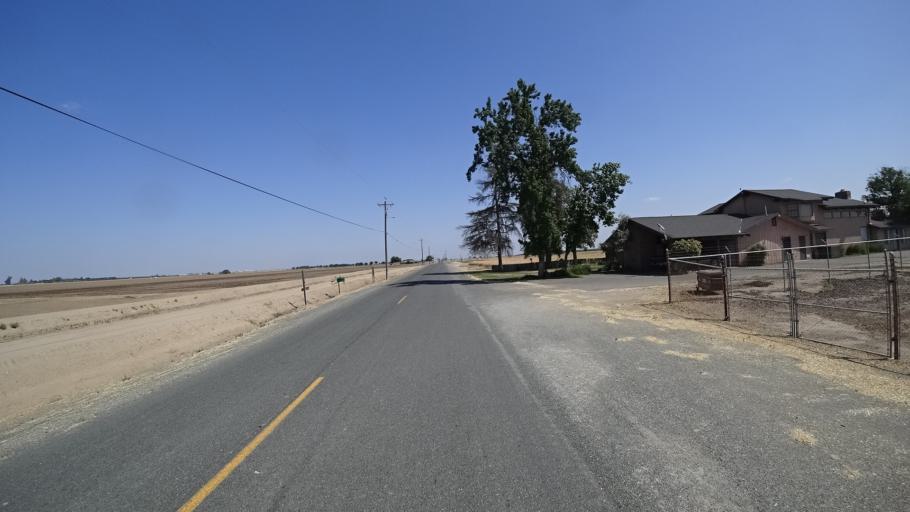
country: US
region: California
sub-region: Kings County
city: Home Garden
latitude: 36.2290
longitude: -119.6189
